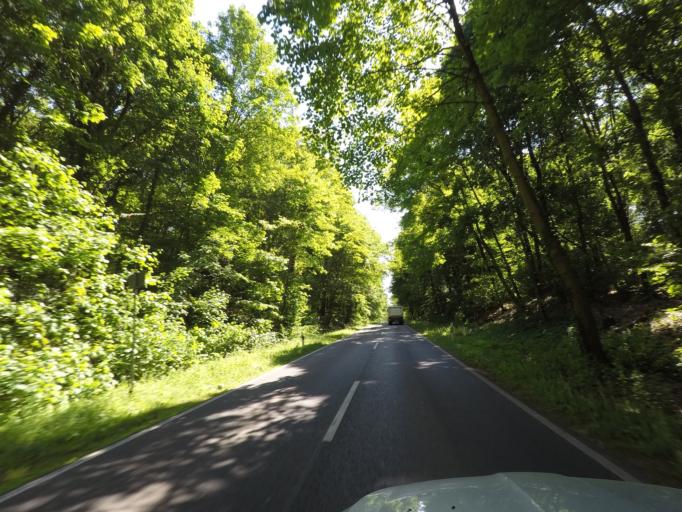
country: DE
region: Brandenburg
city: Eberswalde
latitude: 52.8255
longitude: 13.8310
